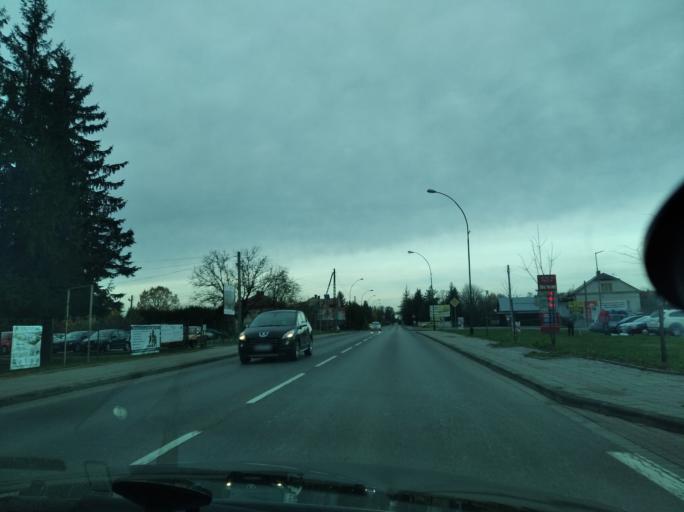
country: PL
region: Subcarpathian Voivodeship
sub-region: Powiat lancucki
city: Lancut
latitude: 50.0913
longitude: 22.2316
